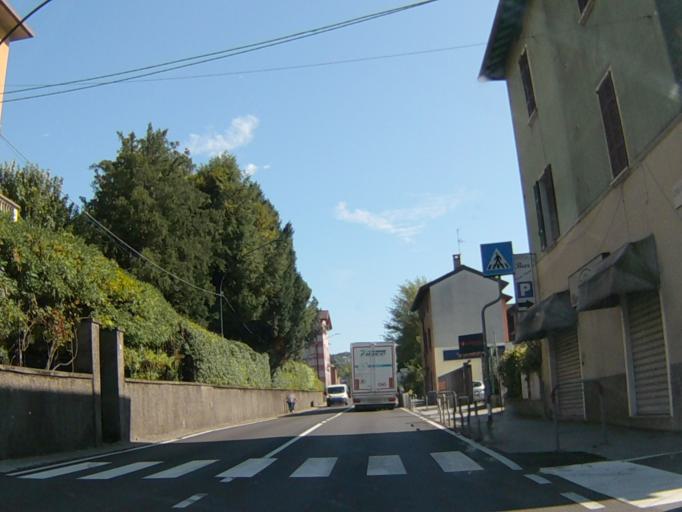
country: IT
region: Lombardy
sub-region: Provincia di Lecco
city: Calolziocorte
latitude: 45.7957
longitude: 9.4355
